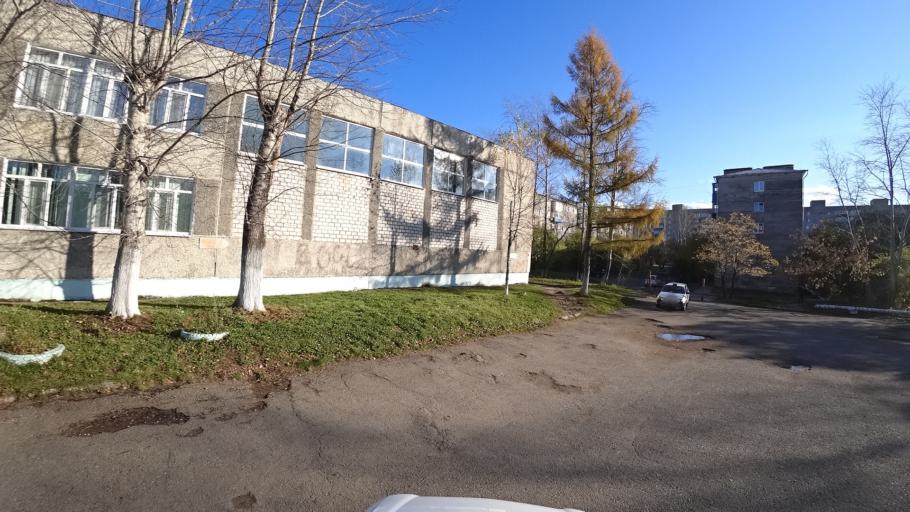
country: RU
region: Khabarovsk Krai
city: Amursk
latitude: 50.2304
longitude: 136.9081
